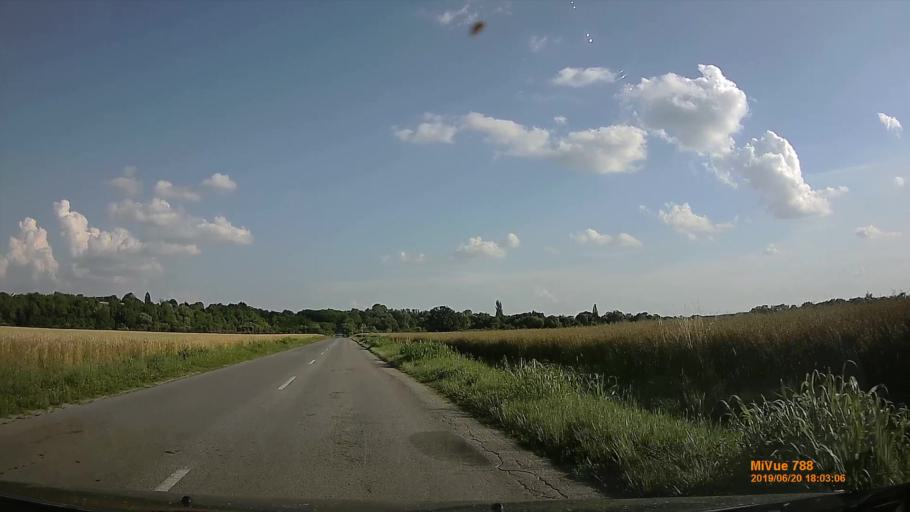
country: HU
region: Baranya
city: Szentlorinc
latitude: 46.0662
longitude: 17.9907
